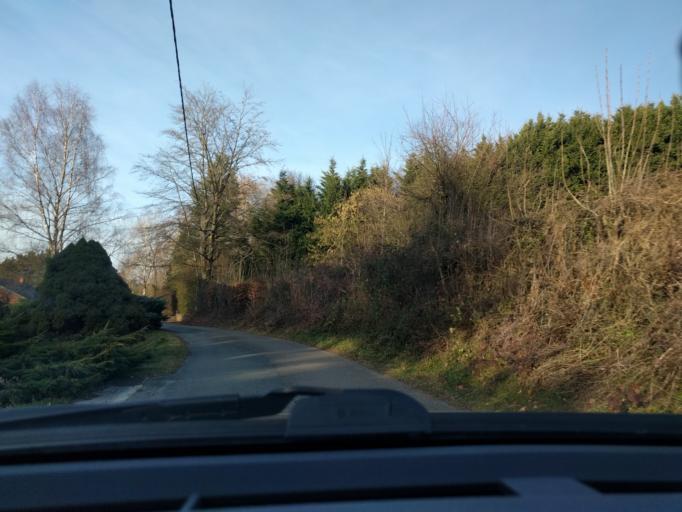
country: BE
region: Wallonia
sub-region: Province de Namur
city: Couvin
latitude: 50.0400
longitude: 4.5061
